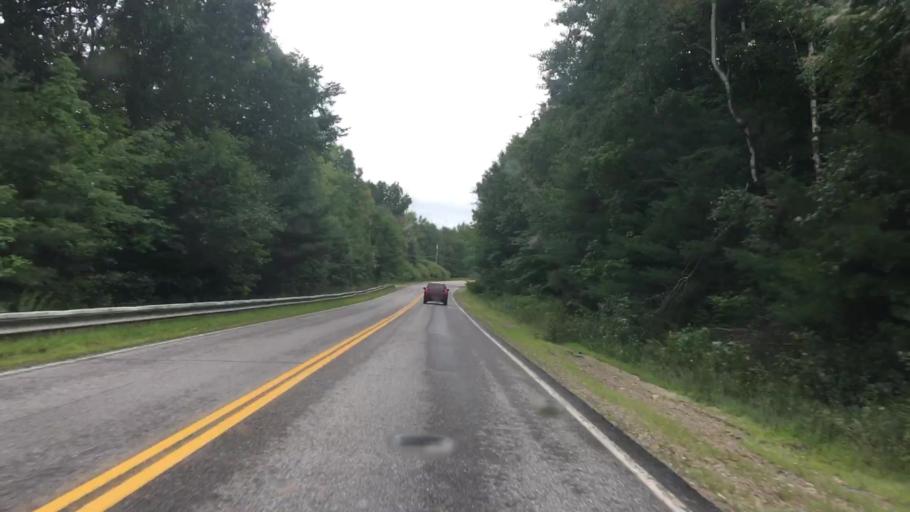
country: US
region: Maine
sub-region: Oxford County
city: Brownfield
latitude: 43.9595
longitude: -70.9004
